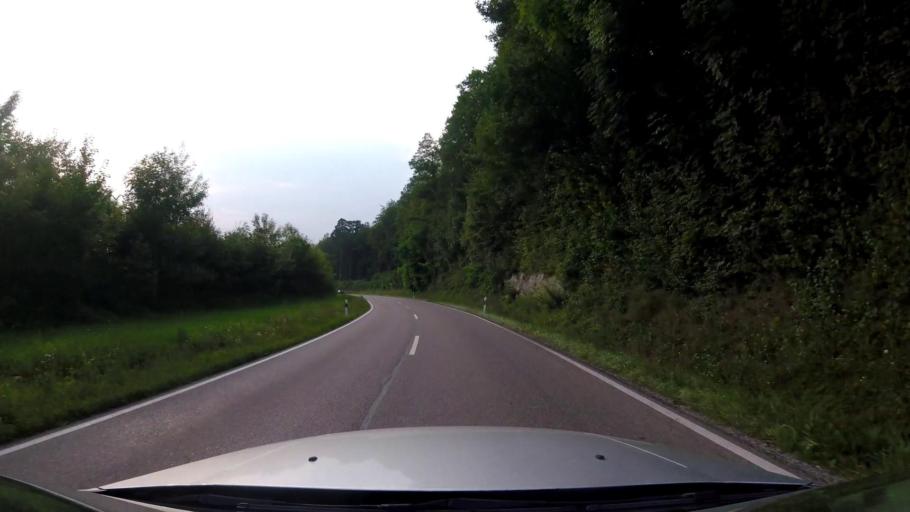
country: DE
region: Baden-Wuerttemberg
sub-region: Regierungsbezirk Stuttgart
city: Urbach
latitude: 48.8578
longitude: 9.5887
